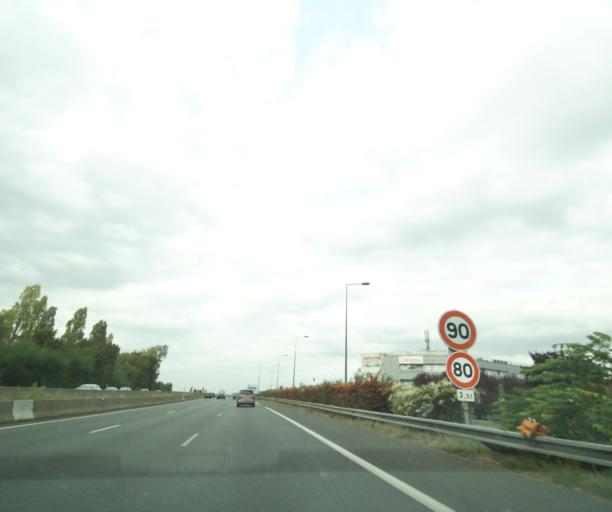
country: FR
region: Centre
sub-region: Departement d'Indre-et-Loire
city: Saint-Avertin
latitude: 47.3705
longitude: 0.7156
